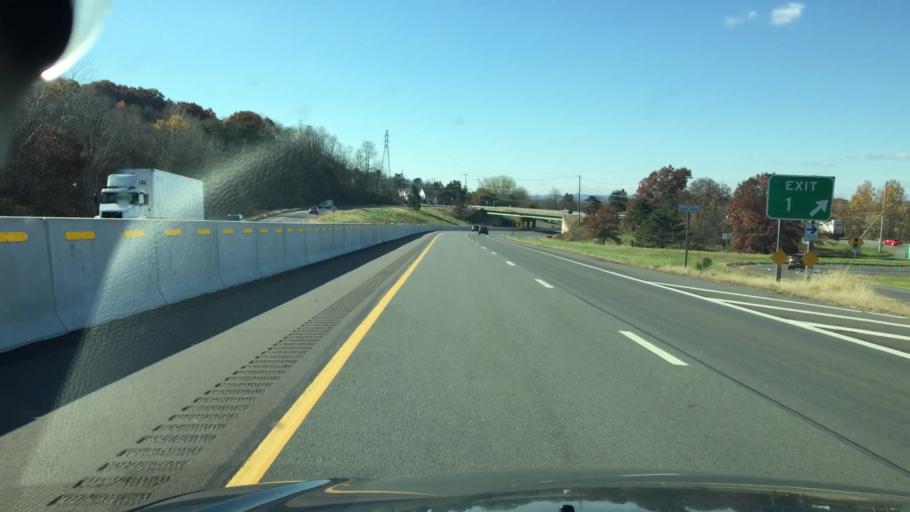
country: US
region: Pennsylvania
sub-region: Luzerne County
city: Ashley
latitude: 41.2001
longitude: -75.9168
